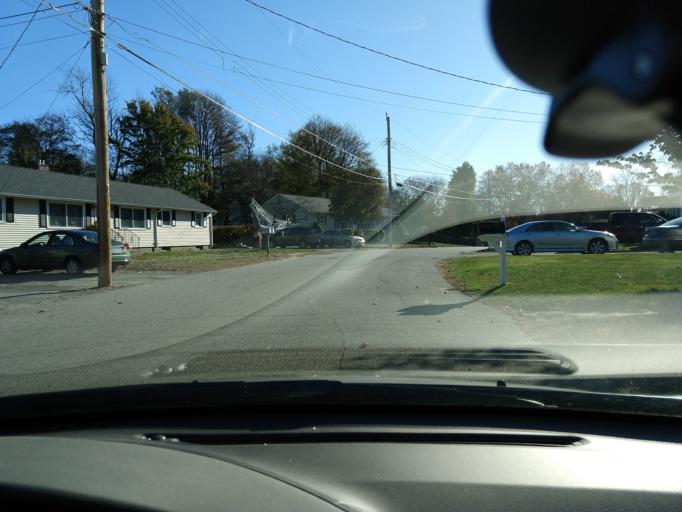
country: US
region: Massachusetts
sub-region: Middlesex County
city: Bedford
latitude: 42.4739
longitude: -71.2705
